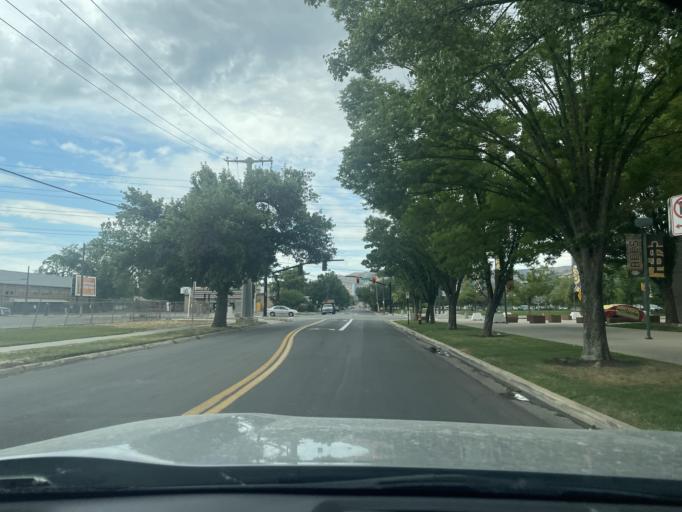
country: US
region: Utah
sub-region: Salt Lake County
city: Salt Lake City
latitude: 40.7409
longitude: -111.8939
